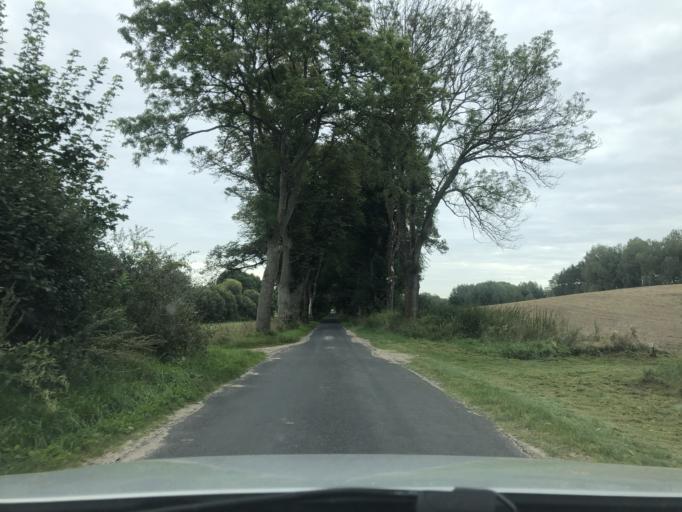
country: PL
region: Greater Poland Voivodeship
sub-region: Powiat pilski
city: Szydlowo
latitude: 53.2706
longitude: 16.6714
